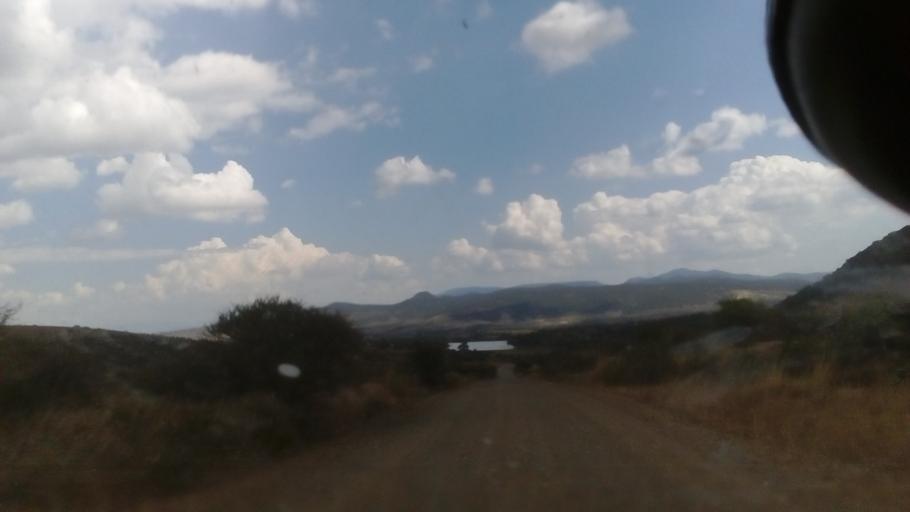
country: MX
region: Guanajuato
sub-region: Leon
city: Lucio Blanco (Los Gavilanes)
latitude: 21.1941
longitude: -101.4608
